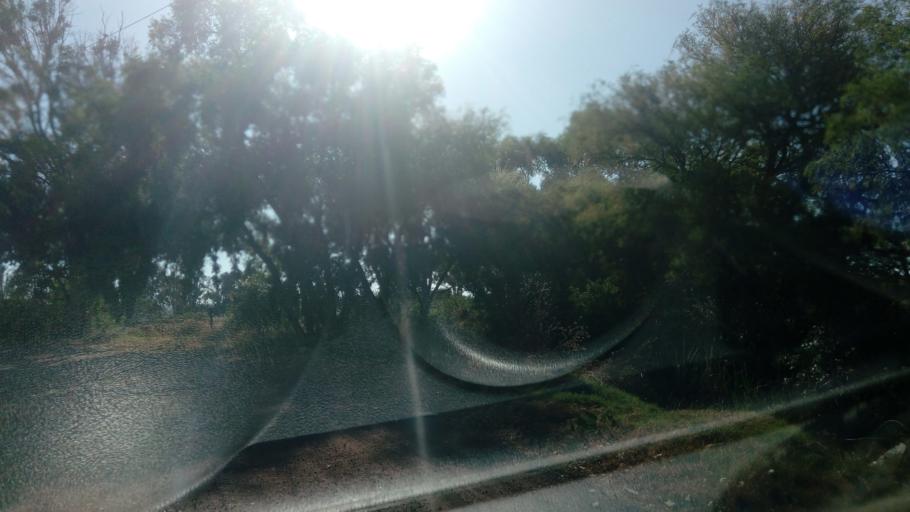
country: MX
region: Durango
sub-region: Durango
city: Jose Refugio Salcido
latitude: 24.0184
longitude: -104.5527
